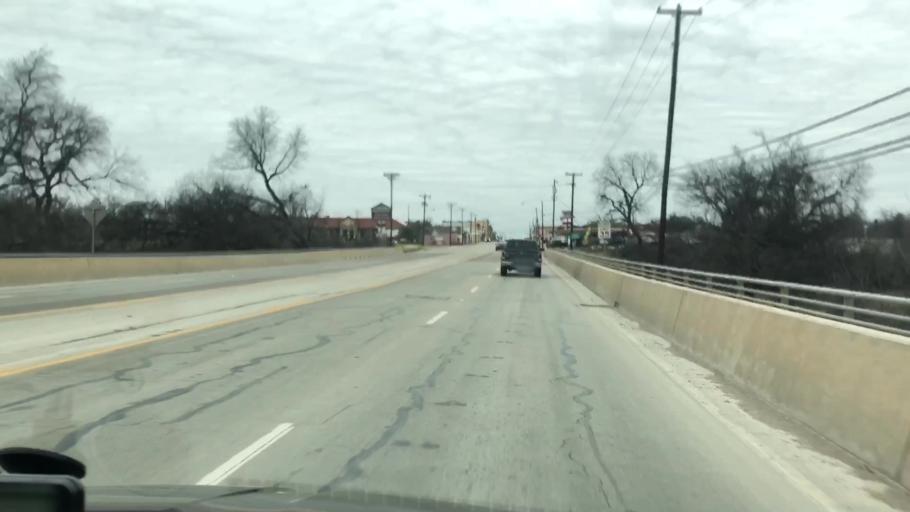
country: US
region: Texas
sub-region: Jack County
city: Jacksboro
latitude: 33.2134
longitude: -98.1588
